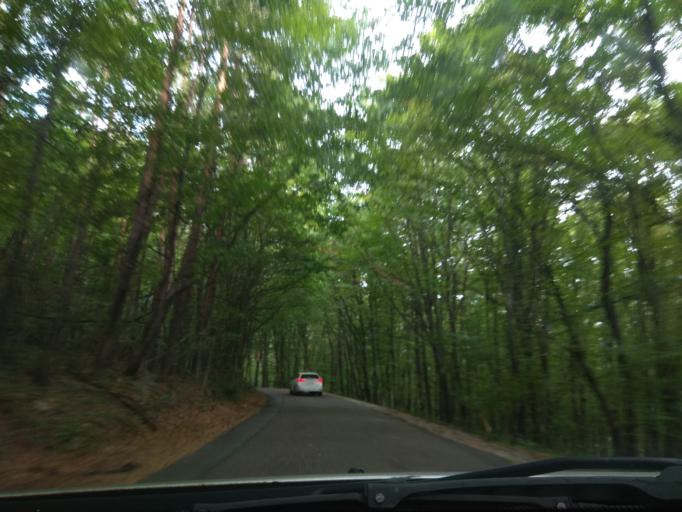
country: HU
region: Borsod-Abauj-Zemplen
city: Sajobabony
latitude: 48.0692
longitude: 20.6696
